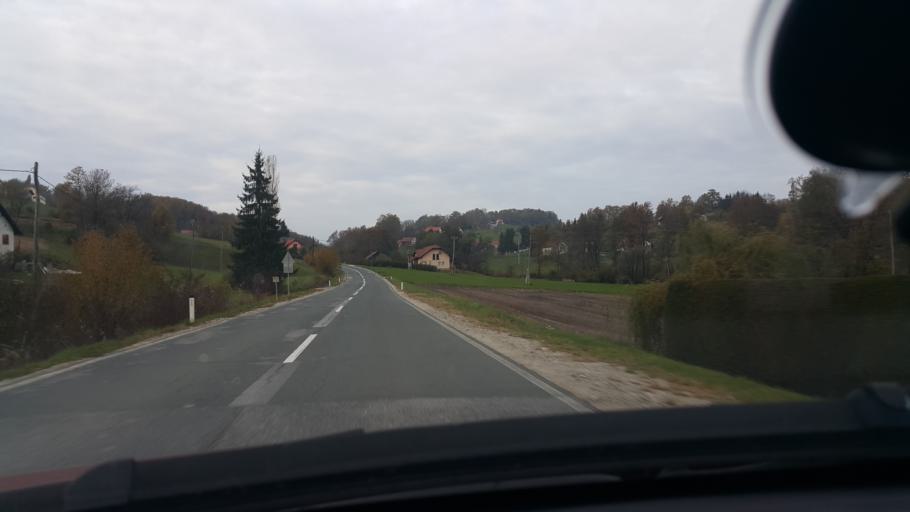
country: SI
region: Bistrica ob Sotli
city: Bistrica ob Sotli
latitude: 46.0644
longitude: 15.6517
